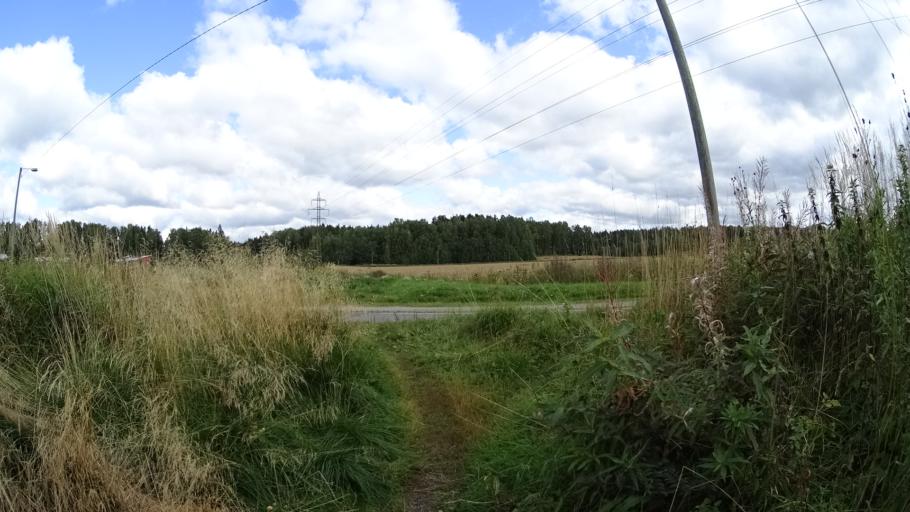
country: FI
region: Uusimaa
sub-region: Helsinki
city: Kilo
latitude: 60.2260
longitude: 24.7868
